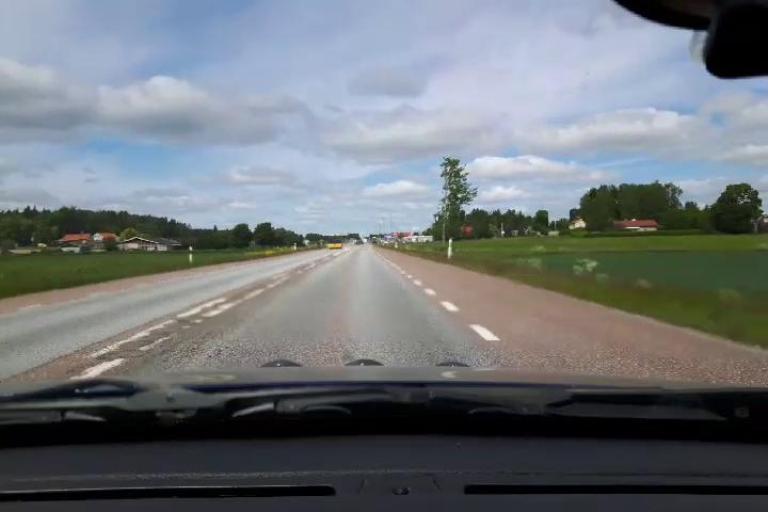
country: SE
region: Uppsala
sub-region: Uppsala Kommun
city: Gamla Uppsala
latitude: 59.9307
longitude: 17.5977
